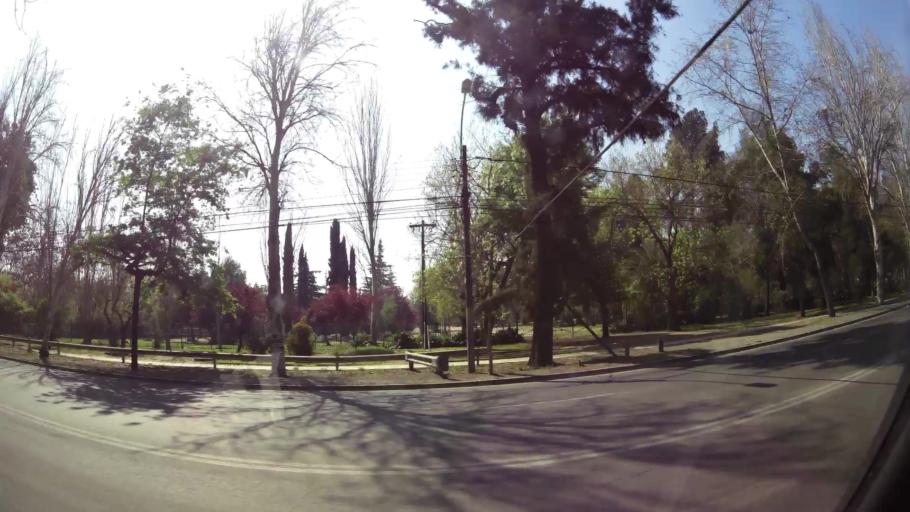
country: CL
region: Santiago Metropolitan
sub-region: Provincia de Santiago
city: Santiago
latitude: -33.4440
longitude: -70.6822
